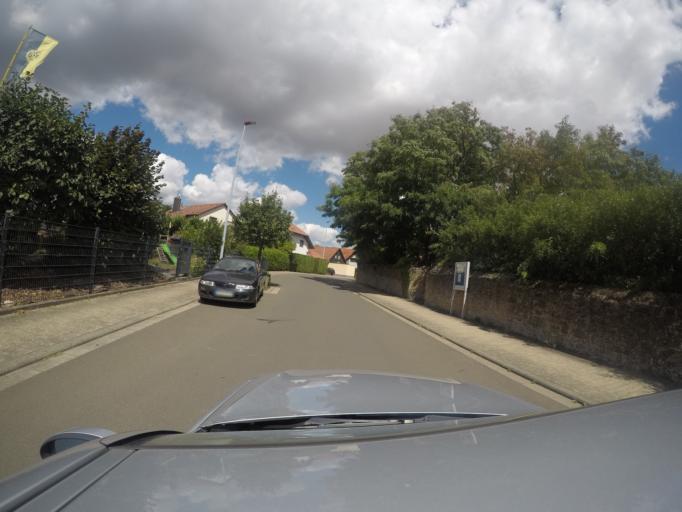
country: DE
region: Rheinland-Pfalz
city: Orbis
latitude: 49.6754
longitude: 7.9873
